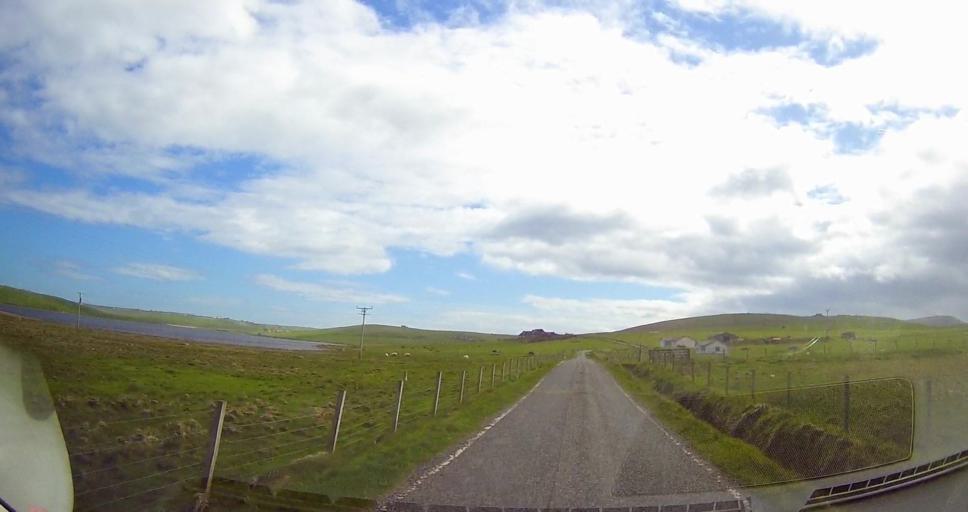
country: GB
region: Scotland
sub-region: Shetland Islands
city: Sandwick
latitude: 59.9360
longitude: -1.3459
